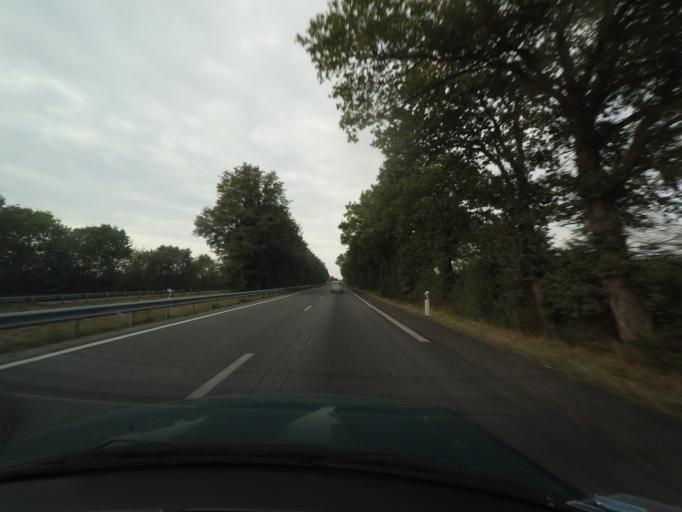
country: FR
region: Brittany
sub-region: Departement d'Ille-et-Vilaine
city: Grand-Fougeray
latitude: 47.7164
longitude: -1.7080
